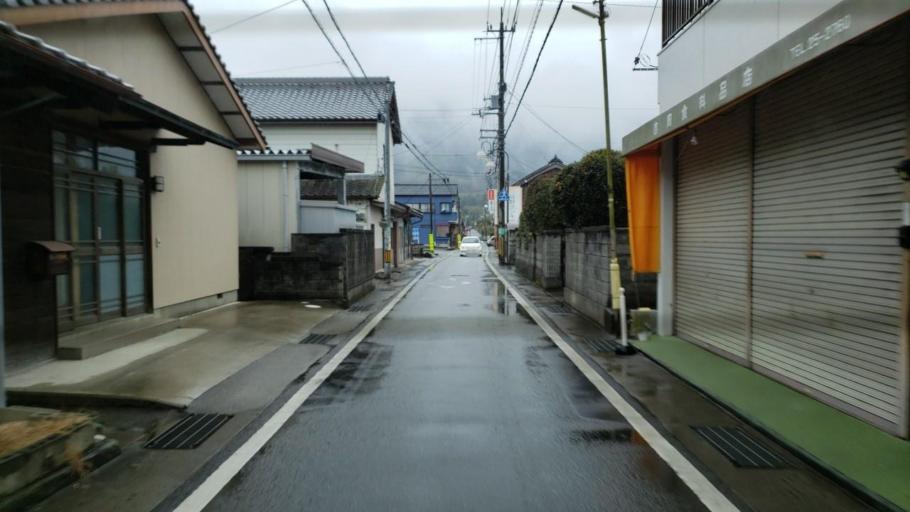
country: JP
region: Tokushima
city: Kamojimacho-jogejima
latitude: 34.0627
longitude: 134.3195
